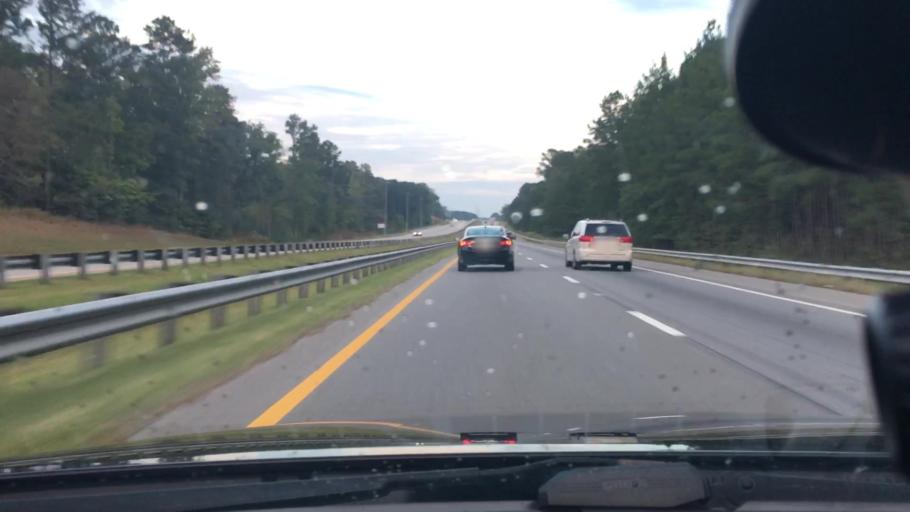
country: US
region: North Carolina
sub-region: Wake County
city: Apex
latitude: 35.6888
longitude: -78.8885
